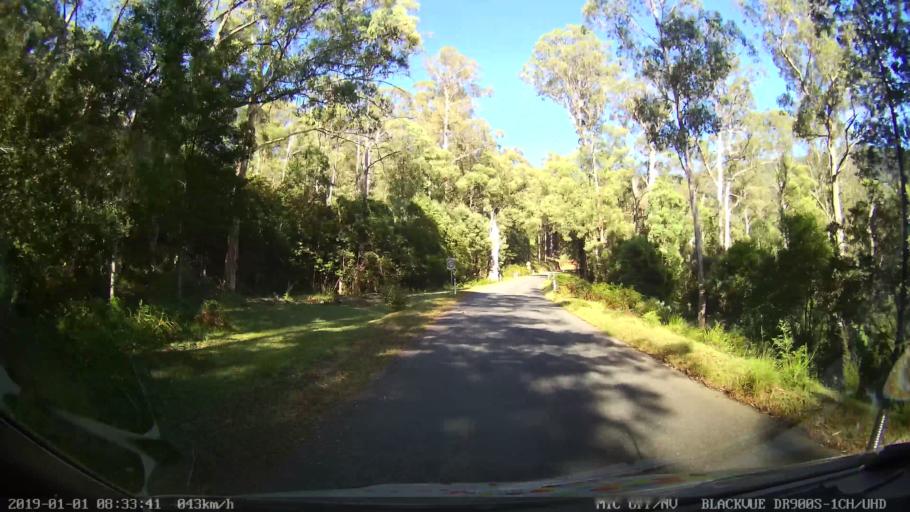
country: AU
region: New South Wales
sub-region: Snowy River
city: Jindabyne
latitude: -36.3548
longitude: 148.2004
